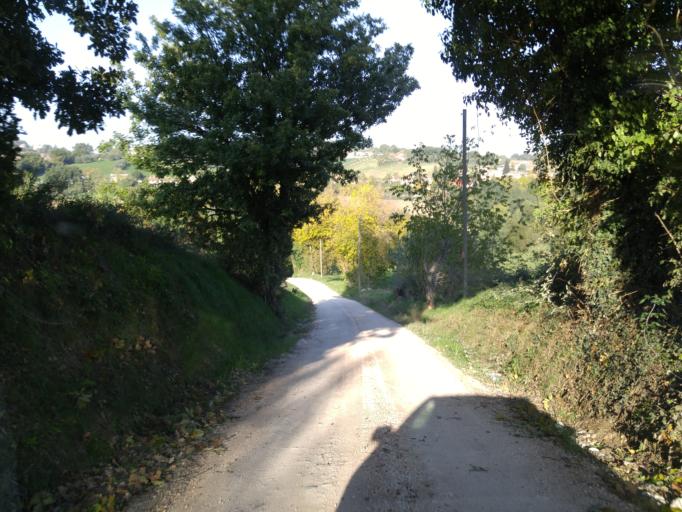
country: IT
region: The Marches
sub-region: Provincia di Pesaro e Urbino
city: Montefelcino
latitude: 43.7213
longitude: 12.8316
